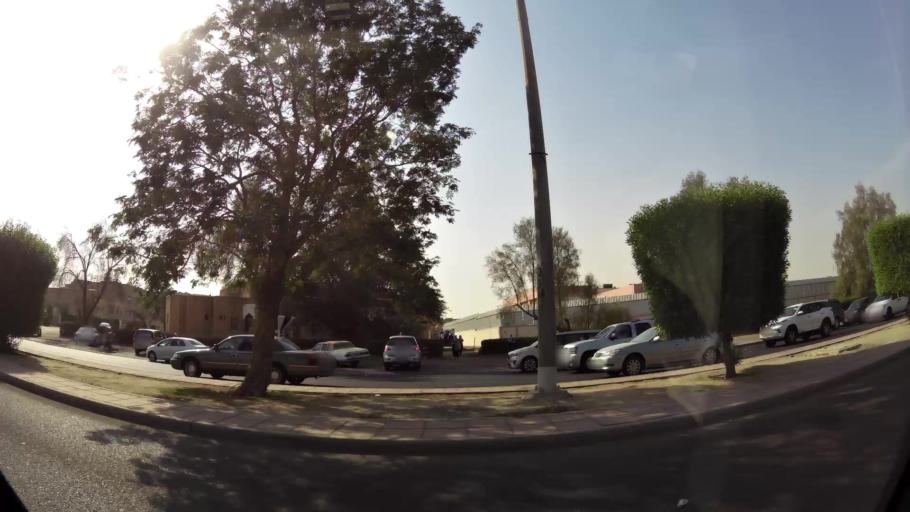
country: KW
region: Al Ahmadi
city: Ar Riqqah
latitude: 29.1636
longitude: 48.0856
